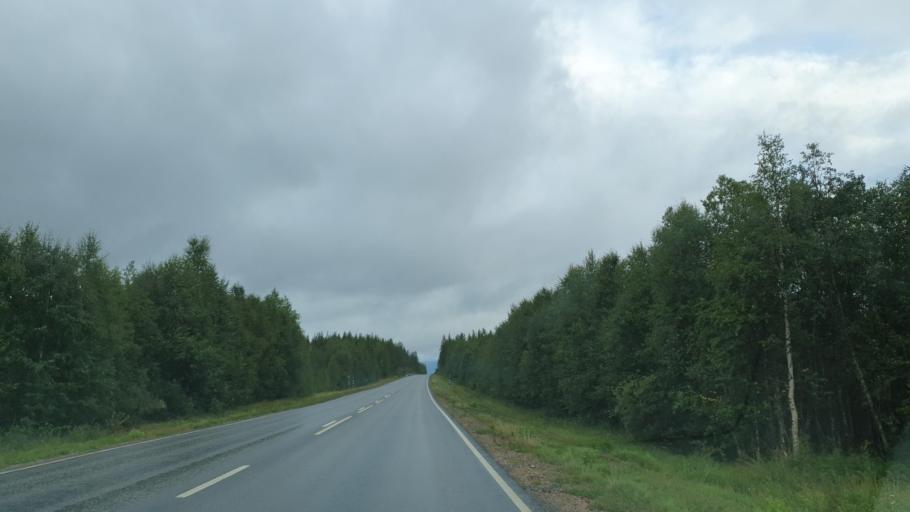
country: FI
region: Lapland
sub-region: Tunturi-Lappi
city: Kolari
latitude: 67.3933
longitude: 23.8065
